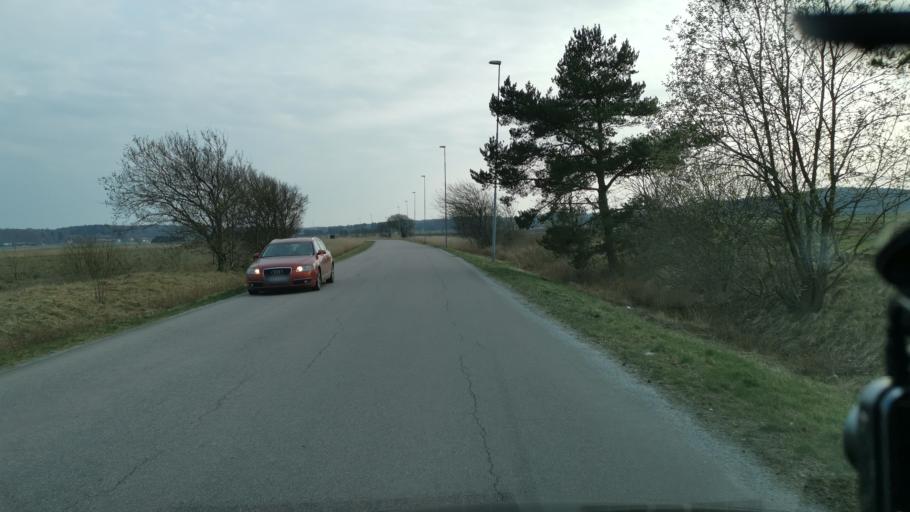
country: SE
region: Vaestra Goetaland
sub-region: Kungalvs Kommun
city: Kode
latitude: 57.9420
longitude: 11.8359
